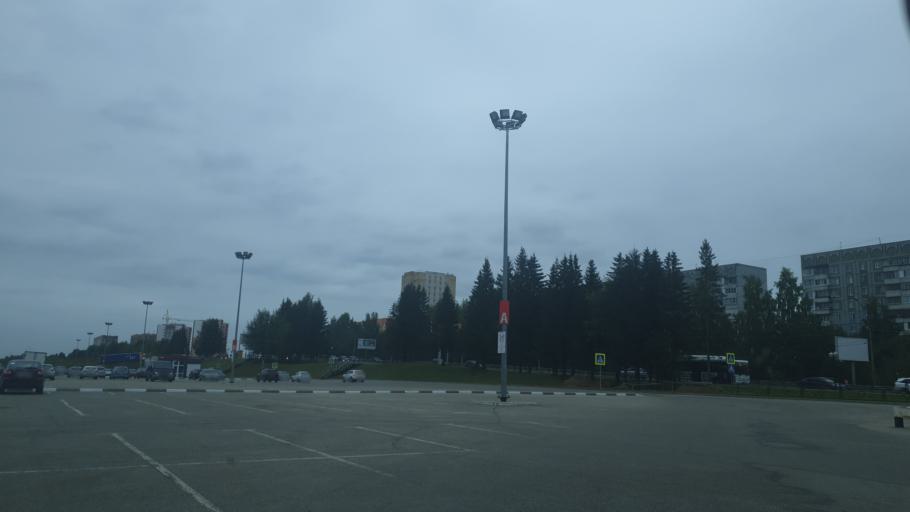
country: RU
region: Komi Republic
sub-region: Syktyvdinskiy Rayon
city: Syktyvkar
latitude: 61.6968
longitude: 50.8041
